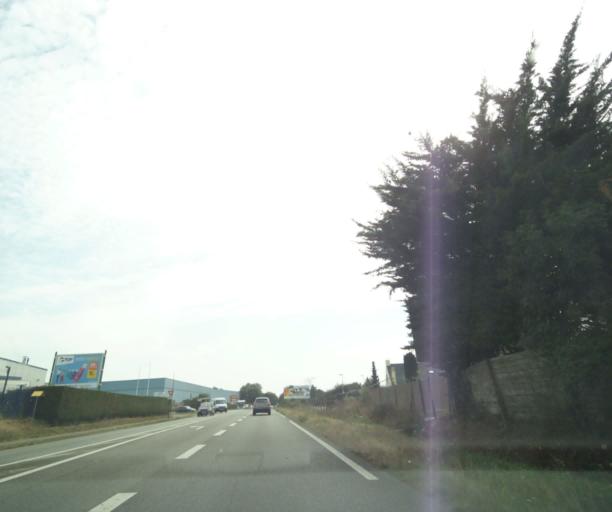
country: FR
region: Pays de la Loire
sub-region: Departement de la Loire-Atlantique
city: Saint-Herblain
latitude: 47.2185
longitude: -1.6487
